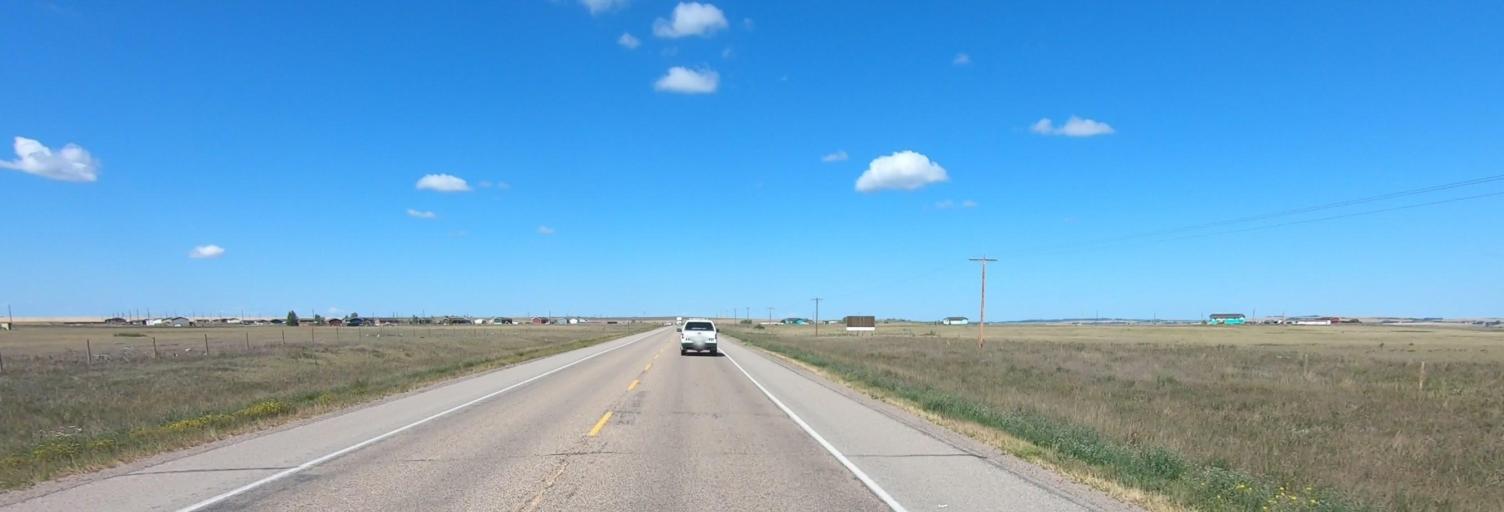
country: CA
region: Alberta
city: Strathmore
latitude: 50.8852
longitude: -113.1828
